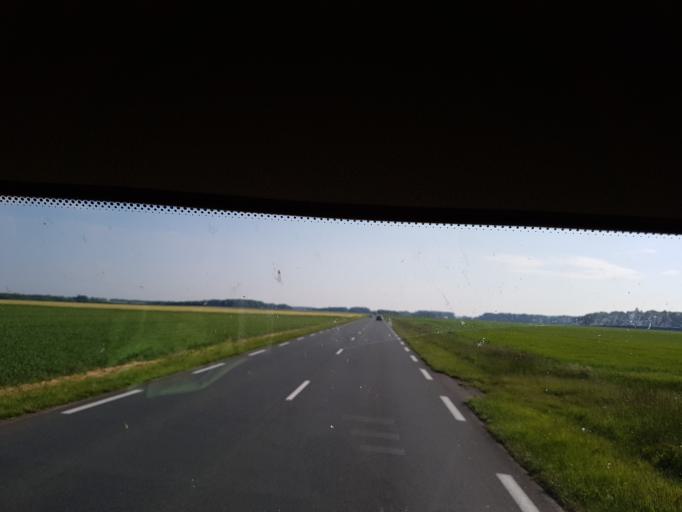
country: FR
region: Picardie
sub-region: Departement de la Somme
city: Crecy-en-Ponthieu
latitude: 50.2049
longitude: 1.8989
